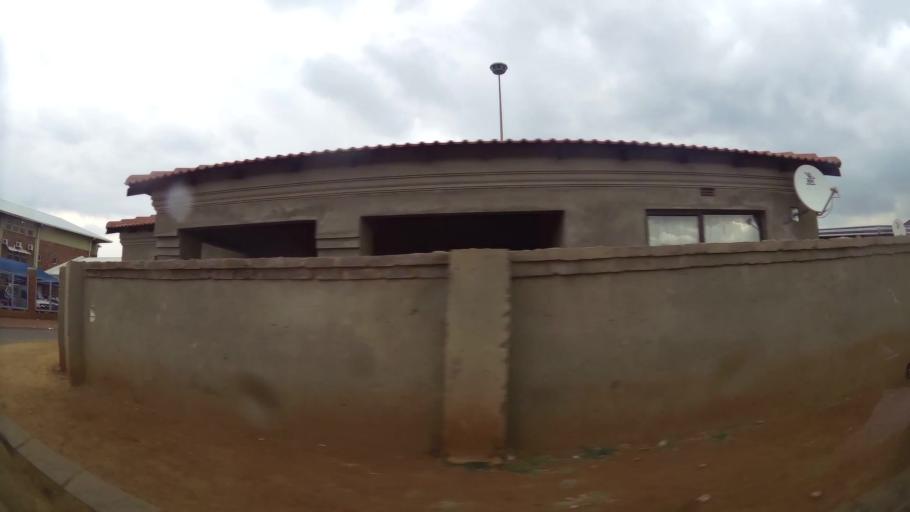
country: ZA
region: Gauteng
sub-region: Ekurhuleni Metropolitan Municipality
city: Germiston
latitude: -26.3610
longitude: 28.1568
